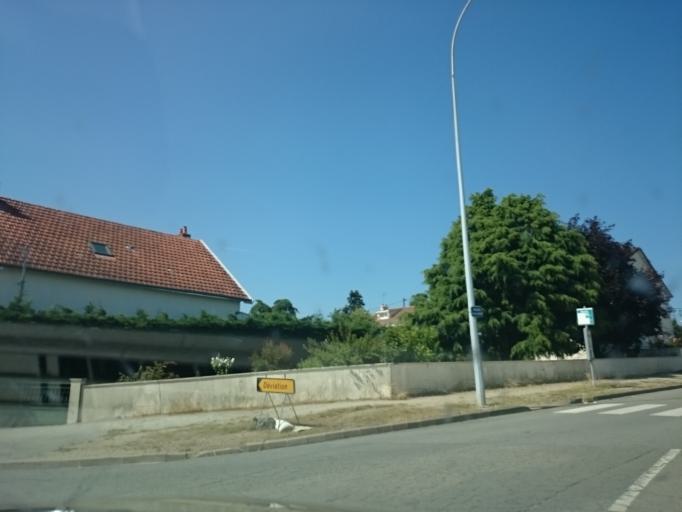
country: FR
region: Pays de la Loire
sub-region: Departement de la Loire-Atlantique
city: Coueron
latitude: 47.2130
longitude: -1.7351
